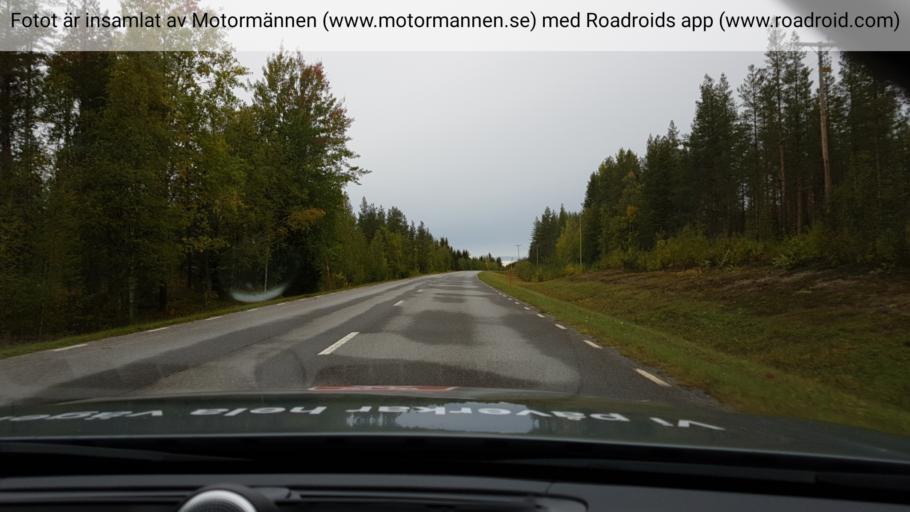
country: SE
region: Jaemtland
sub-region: Stroemsunds Kommun
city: Stroemsund
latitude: 64.2574
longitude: 15.4035
